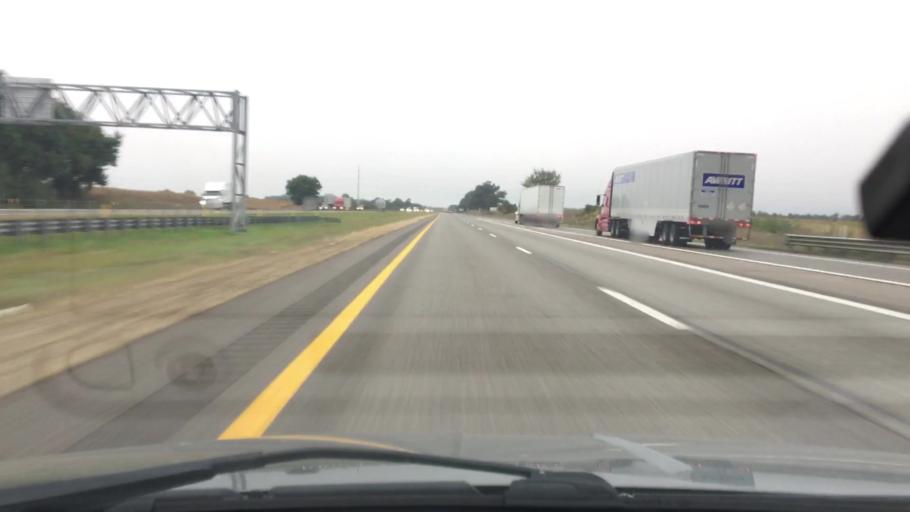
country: US
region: Michigan
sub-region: Calhoun County
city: Marshall
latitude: 42.2975
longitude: -85.0050
